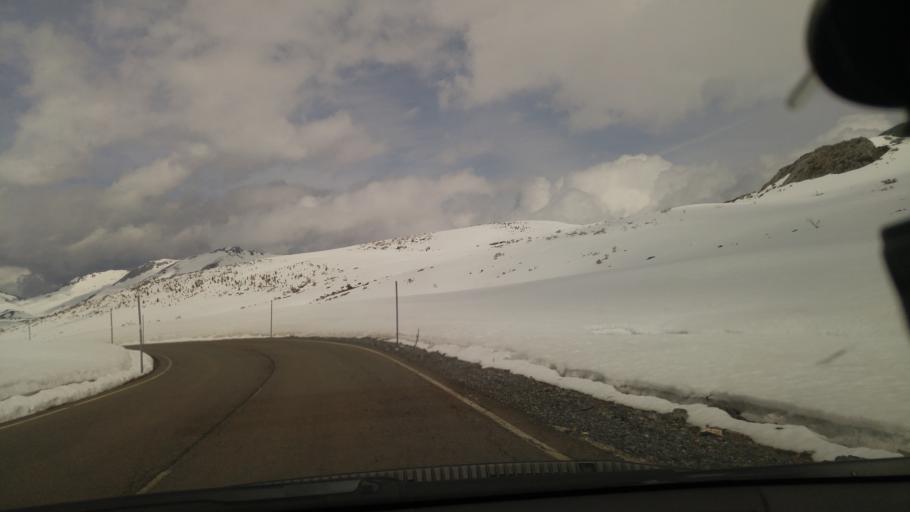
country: ES
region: Castille and Leon
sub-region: Provincia de Leon
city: Puebla de Lillo
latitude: 43.0472
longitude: -5.3772
